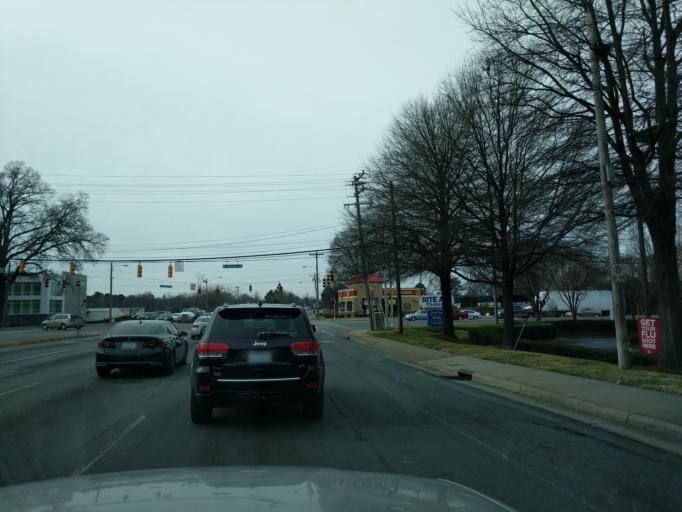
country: US
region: North Carolina
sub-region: Mecklenburg County
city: Charlotte
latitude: 35.1973
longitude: -80.7910
